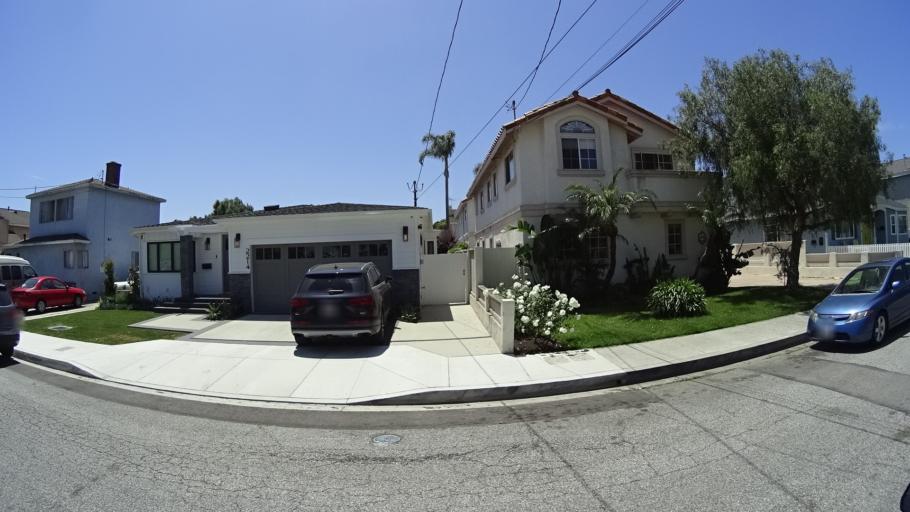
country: US
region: California
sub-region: Los Angeles County
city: Lawndale
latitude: 33.8847
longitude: -118.3715
